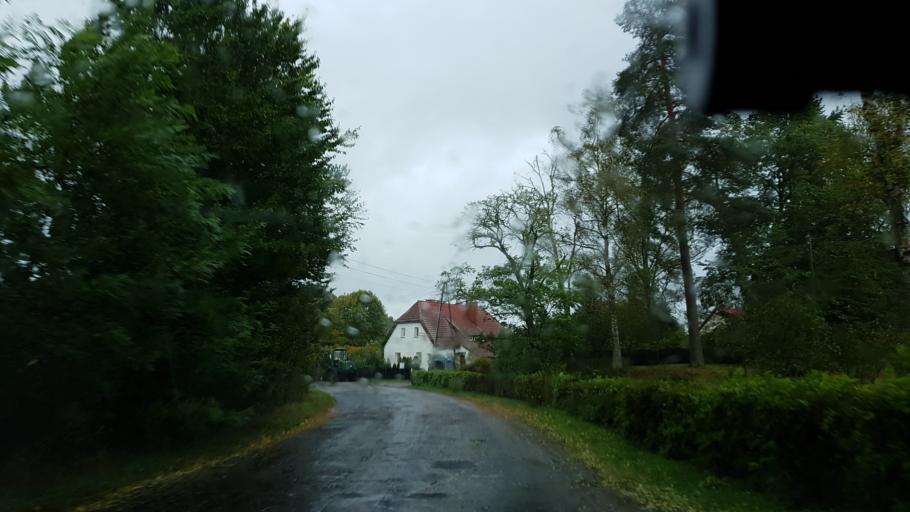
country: PL
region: West Pomeranian Voivodeship
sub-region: Powiat goleniowski
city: Stepnica
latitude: 53.6806
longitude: 14.7157
